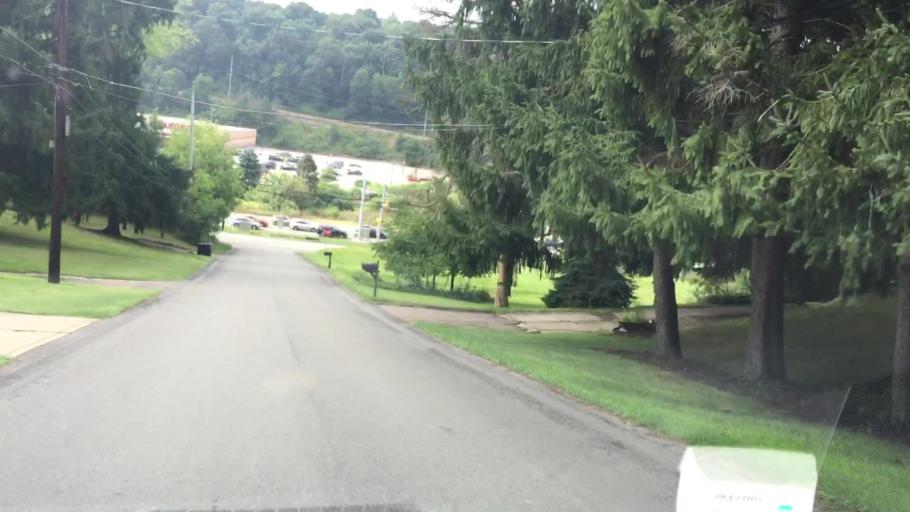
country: US
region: Pennsylvania
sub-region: Allegheny County
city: Franklin Park
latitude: 40.5881
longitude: -80.0409
